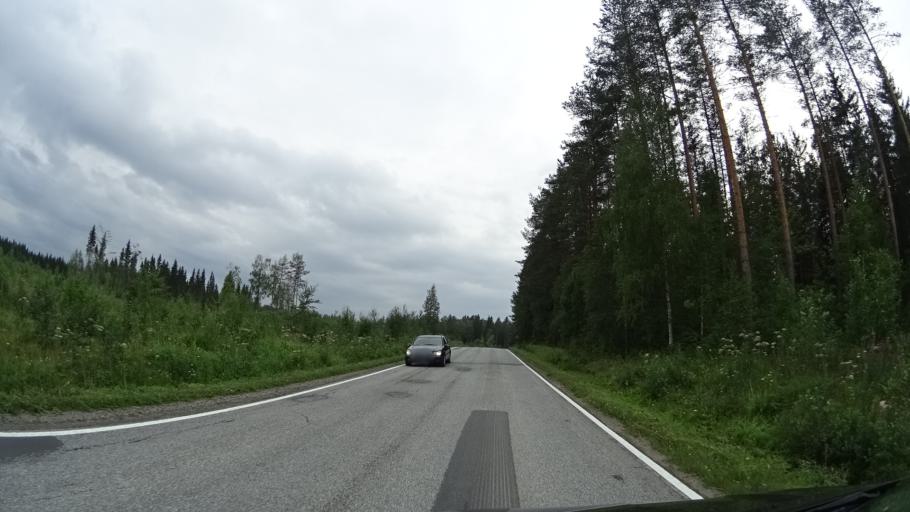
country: FI
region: Southern Savonia
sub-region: Savonlinna
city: Punkaharju
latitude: 61.7487
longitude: 29.5057
